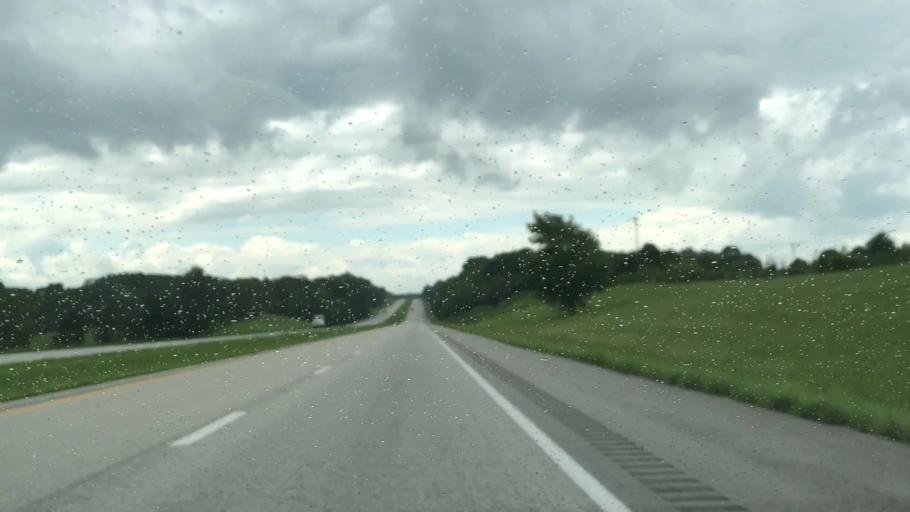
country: US
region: Kentucky
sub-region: Russell County
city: Russell Springs
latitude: 37.0720
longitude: -85.0156
